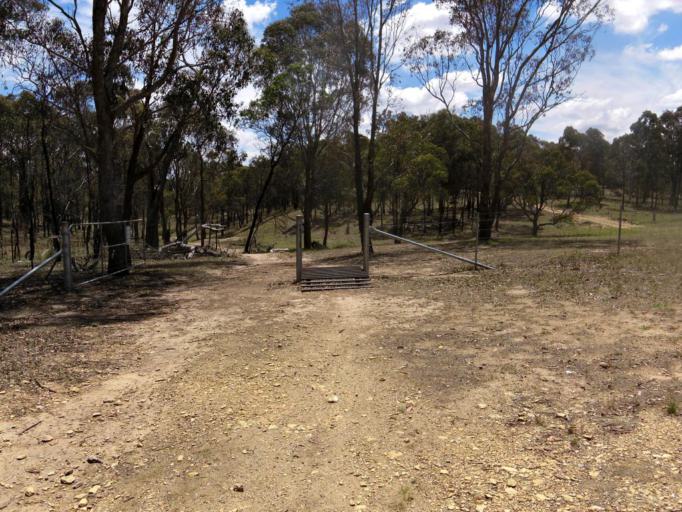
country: AU
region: Australian Capital Territory
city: Kaleen
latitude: -35.1371
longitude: 149.1463
